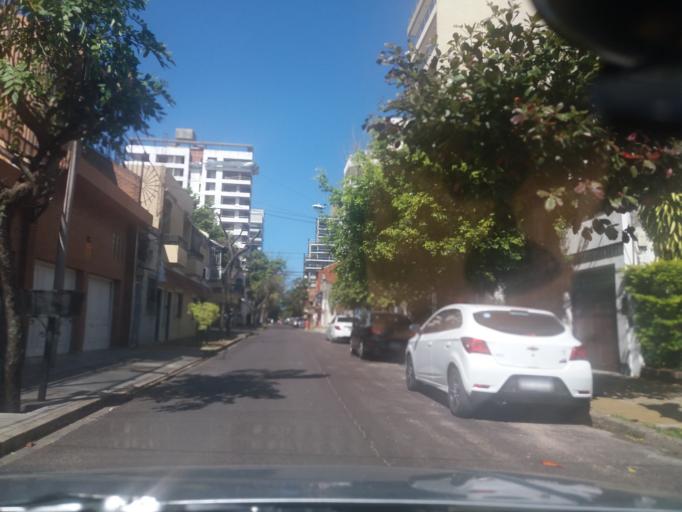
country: AR
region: Corrientes
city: Corrientes
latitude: -27.4664
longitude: -58.8467
